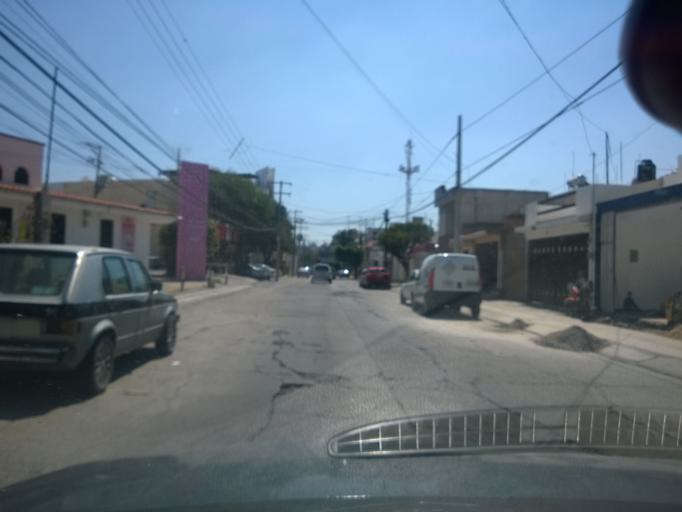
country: MX
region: Guanajuato
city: Leon
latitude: 21.1542
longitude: -101.6900
